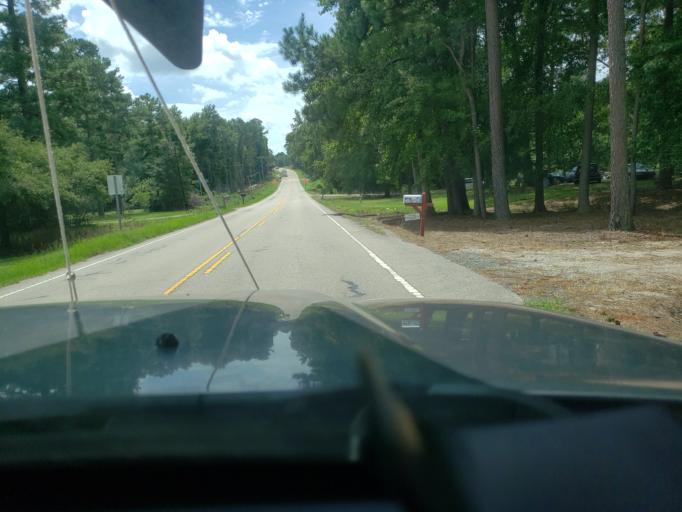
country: US
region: North Carolina
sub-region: Wake County
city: Rolesville
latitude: 35.8881
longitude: -78.4359
